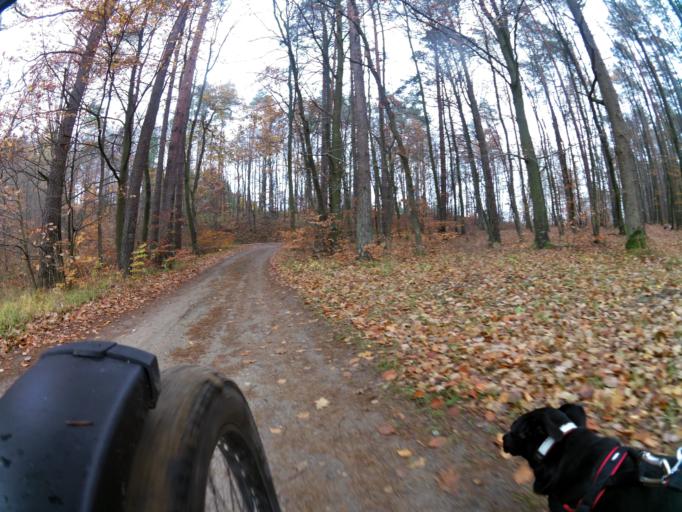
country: PL
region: Pomeranian Voivodeship
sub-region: Powiat wejherowski
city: Orle
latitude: 54.6880
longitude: 18.1489
